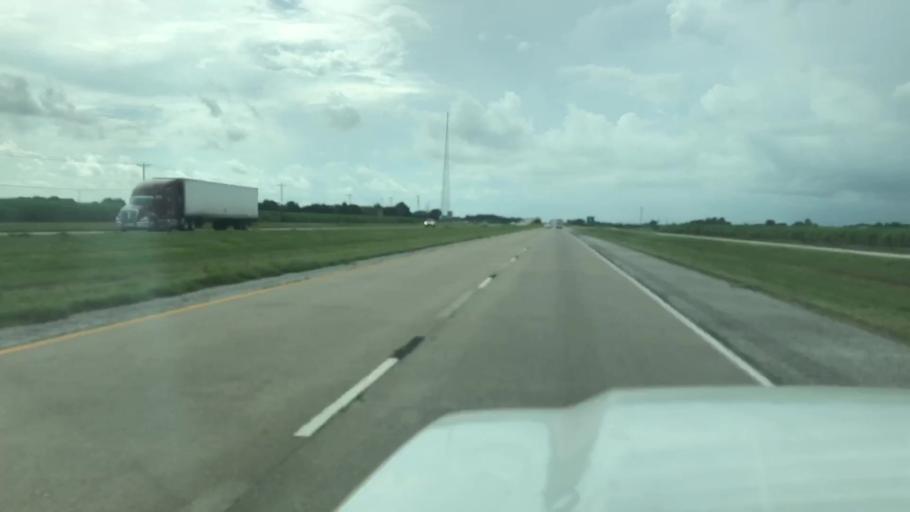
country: US
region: Louisiana
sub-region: Iberia Parish
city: Jeanerette
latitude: 29.9145
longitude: -91.7204
